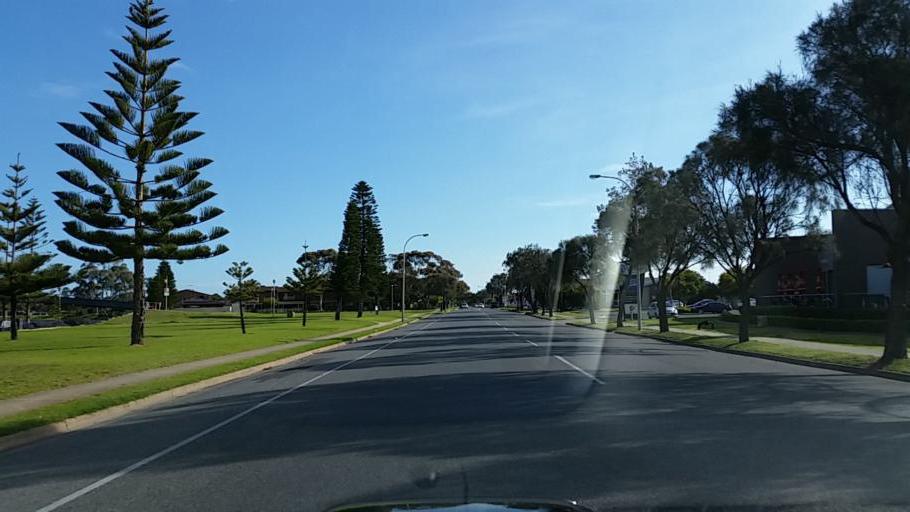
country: AU
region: South Australia
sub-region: Charles Sturt
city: West Lakes Shore
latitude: -34.8598
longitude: 138.4916
